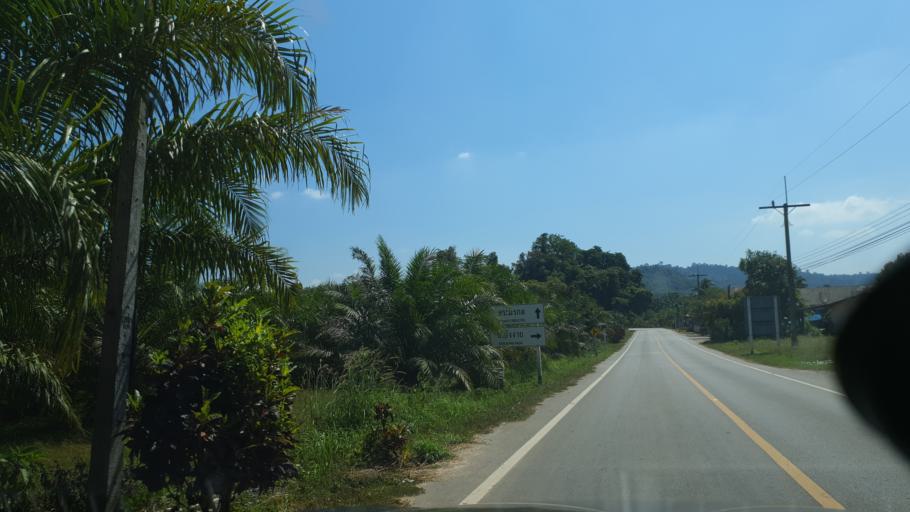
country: TH
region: Krabi
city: Khlong Thom
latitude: 7.9364
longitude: 99.2197
